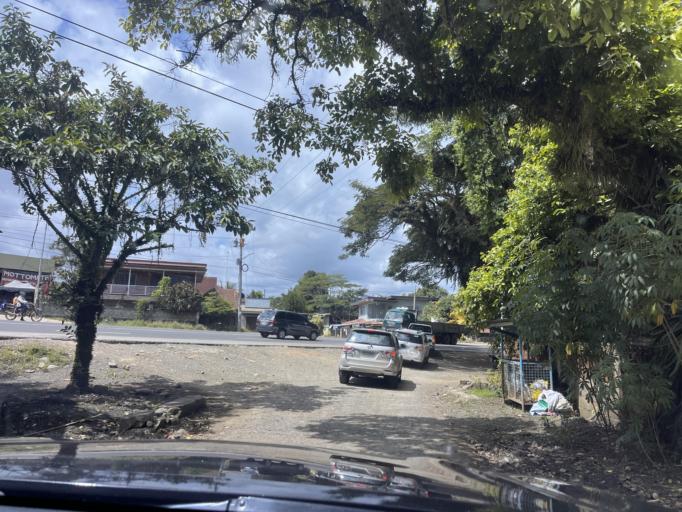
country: PH
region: Northern Mindanao
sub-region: Province of Bukidnon
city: Impalutao
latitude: 8.2706
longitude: 125.0169
